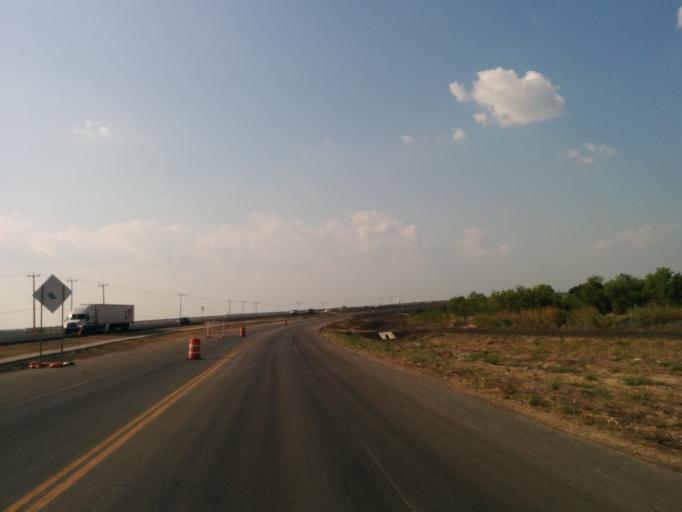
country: US
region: Texas
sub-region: Bexar County
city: Converse
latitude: 29.4783
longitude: -98.2958
